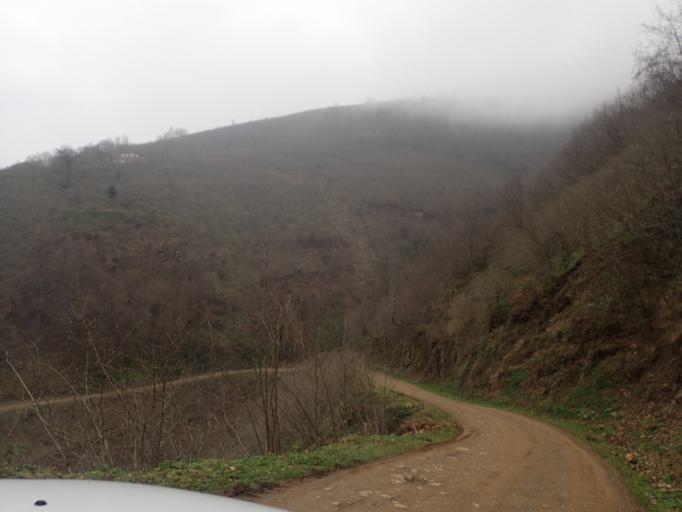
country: TR
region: Ordu
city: Camas
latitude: 40.8965
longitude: 37.5656
